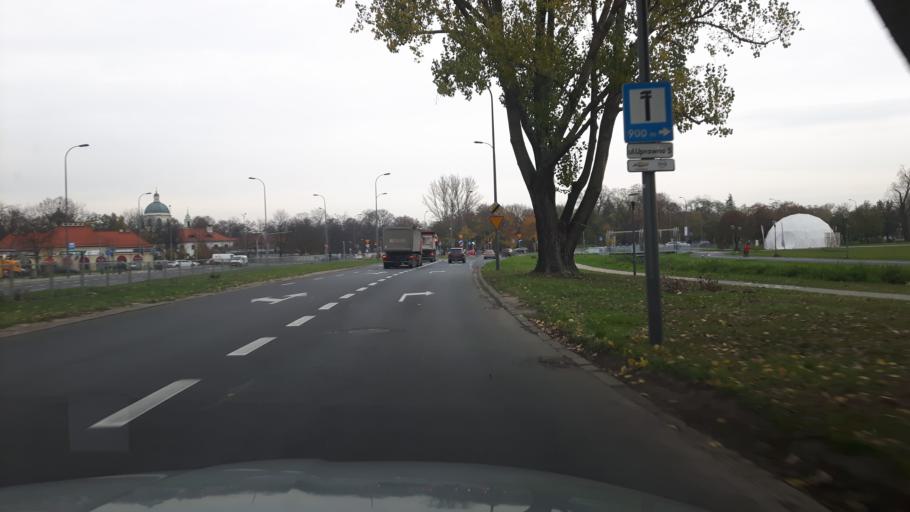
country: PL
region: Masovian Voivodeship
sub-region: Warszawa
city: Wilanow
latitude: 52.1665
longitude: 21.0823
